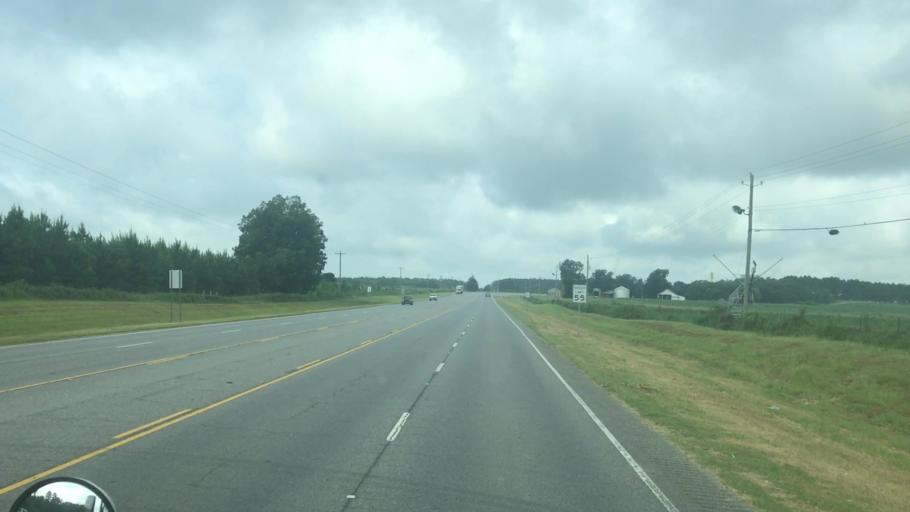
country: US
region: Georgia
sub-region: Miller County
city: Colquitt
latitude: 31.1702
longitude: -84.7464
